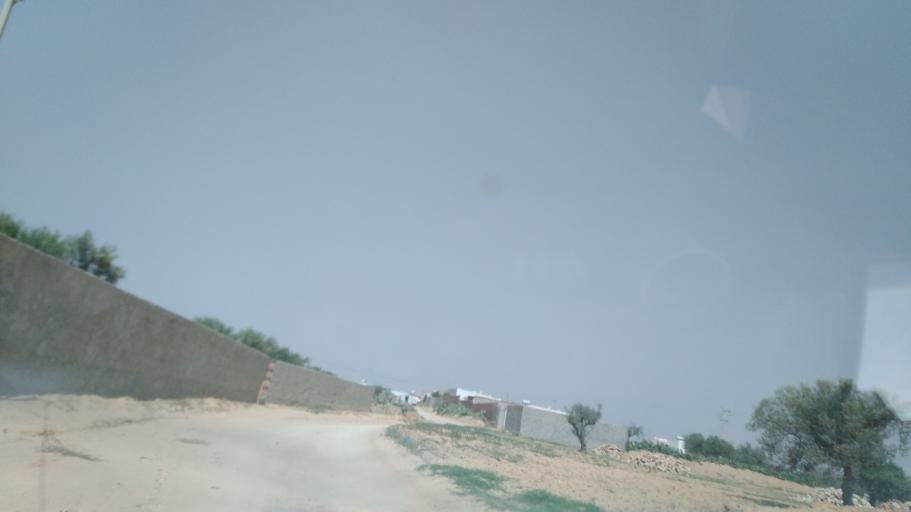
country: TN
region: Safaqis
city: Sfax
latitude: 34.6245
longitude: 10.5762
